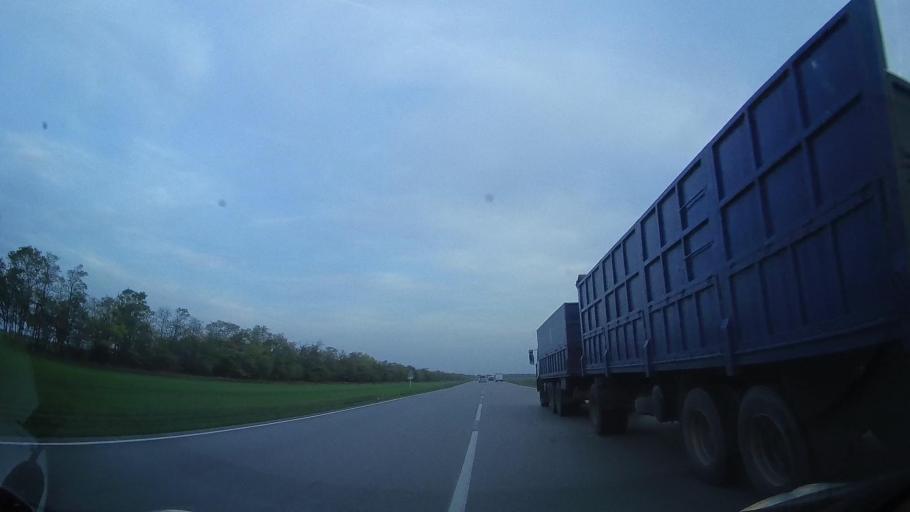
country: RU
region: Rostov
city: Kagal'nitskaya
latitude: 46.9154
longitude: 40.1096
